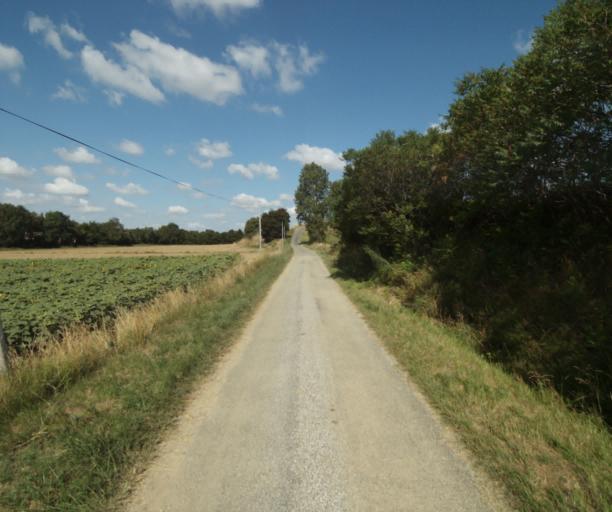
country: FR
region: Midi-Pyrenees
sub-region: Departement de la Haute-Garonne
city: Villefranche-de-Lauragais
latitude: 43.4484
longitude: 1.7771
